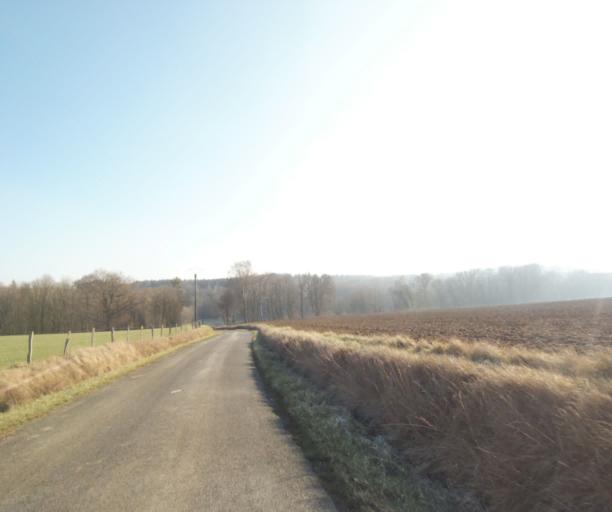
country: FR
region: Champagne-Ardenne
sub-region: Departement de la Haute-Marne
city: Bienville
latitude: 48.5011
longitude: 5.0440
